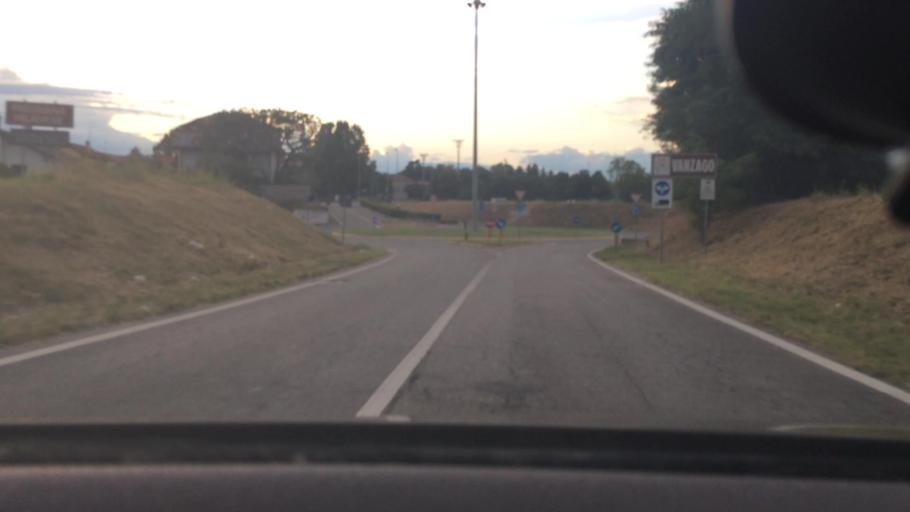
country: IT
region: Lombardy
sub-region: Citta metropolitana di Milano
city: Pregnana Milanese
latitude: 45.5225
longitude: 9.0019
